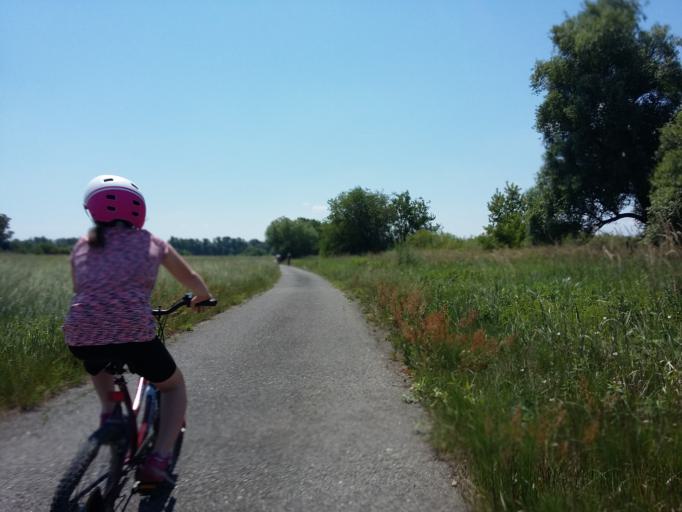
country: AT
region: Lower Austria
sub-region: Politischer Bezirk Ganserndorf
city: Marchegg
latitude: 48.2504
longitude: 16.9520
